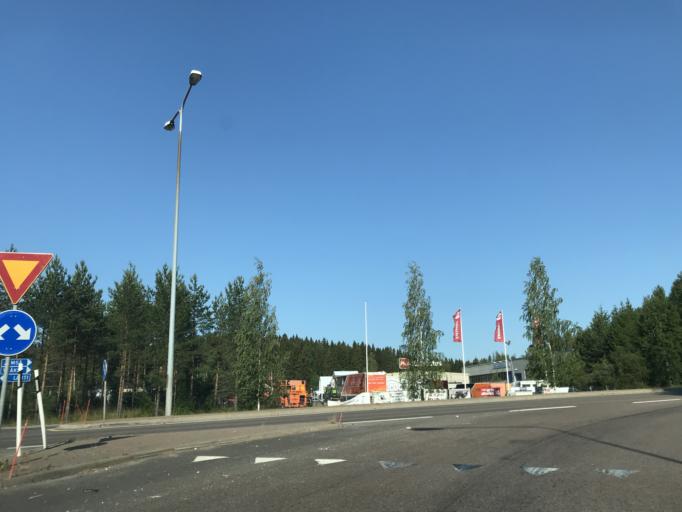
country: FI
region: Paijanne Tavastia
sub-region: Lahti
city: Lahti
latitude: 61.0095
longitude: 25.6832
